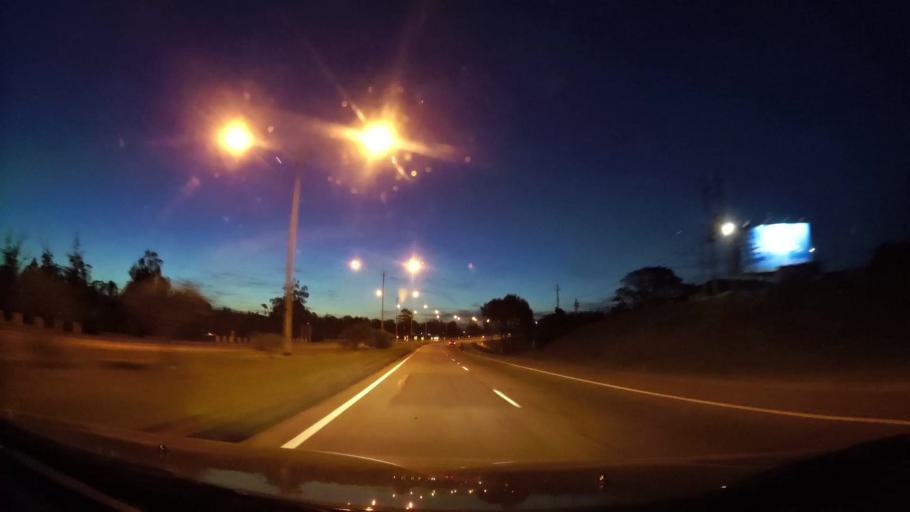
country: UY
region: Canelones
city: Atlantida
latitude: -34.7677
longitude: -55.7715
